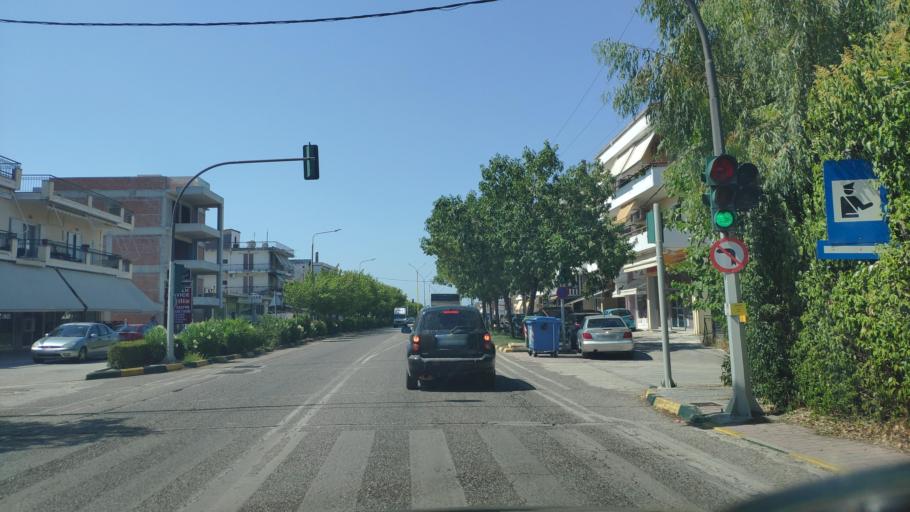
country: GR
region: Epirus
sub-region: Nomos Artas
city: Arta
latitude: 39.1628
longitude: 20.9813
